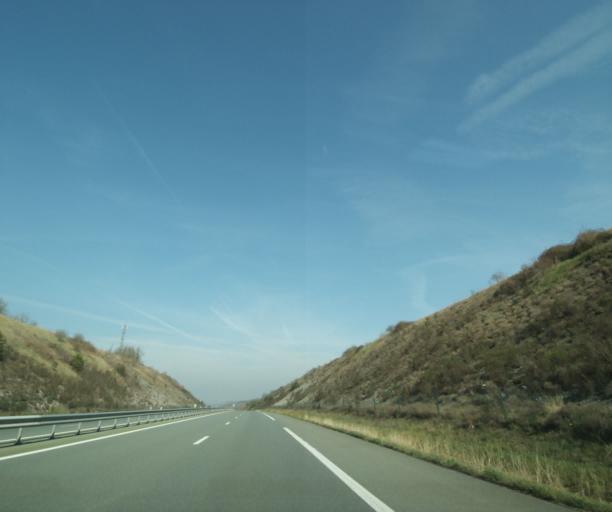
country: FR
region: Midi-Pyrenees
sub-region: Departement du Lot
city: Le Vigan
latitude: 44.7107
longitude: 1.5708
